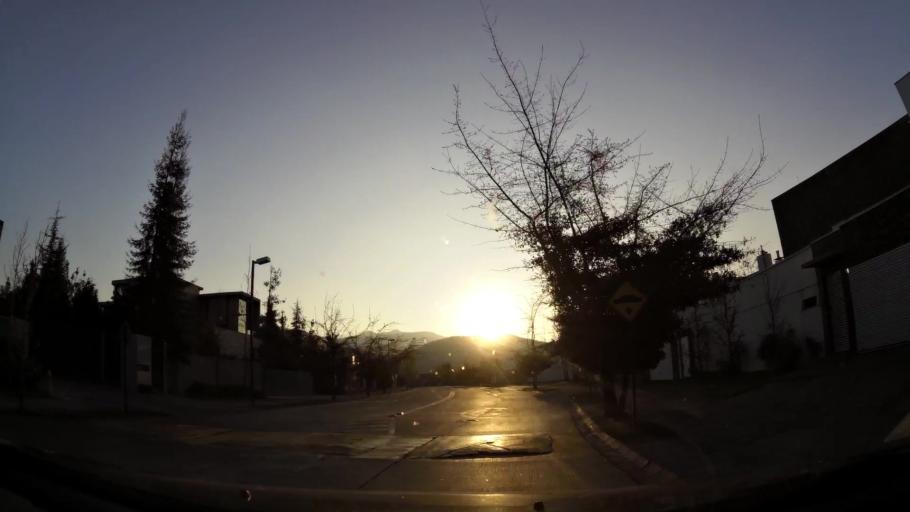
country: CL
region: Santiago Metropolitan
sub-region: Provincia de Chacabuco
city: Chicureo Abajo
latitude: -33.3319
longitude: -70.5352
